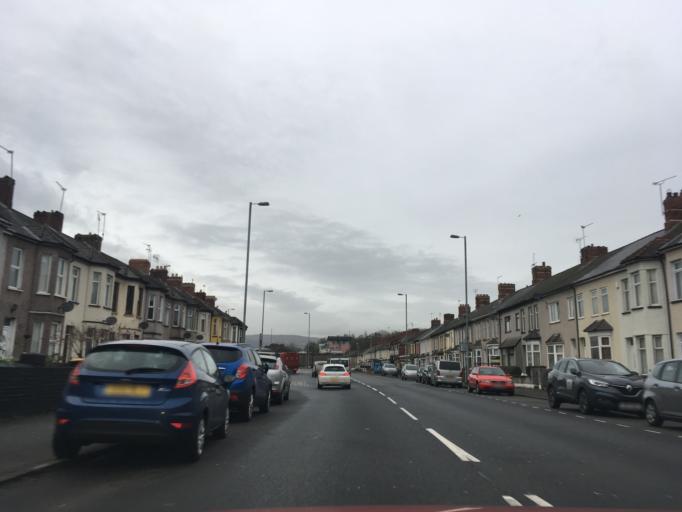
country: GB
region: Wales
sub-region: Newport
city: Newport
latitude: 51.5991
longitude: -3.0010
